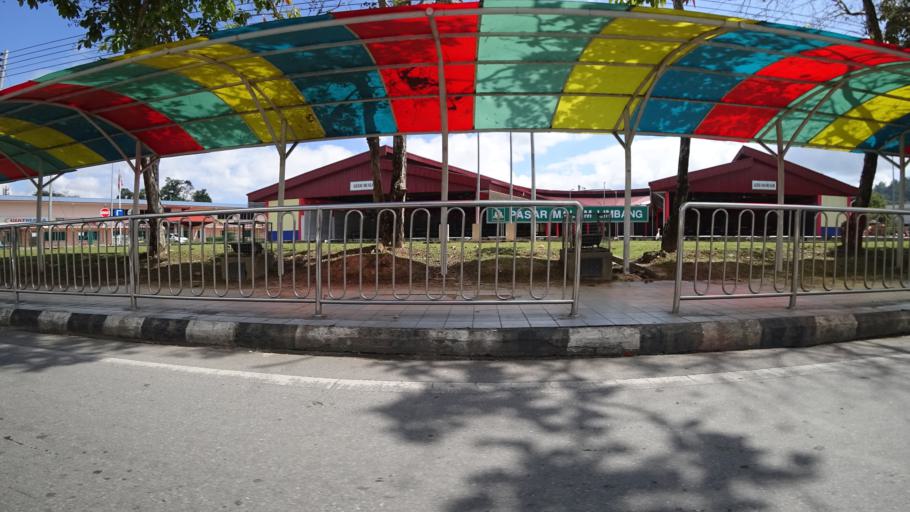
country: MY
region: Sarawak
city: Limbang
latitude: 4.7578
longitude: 115.0069
